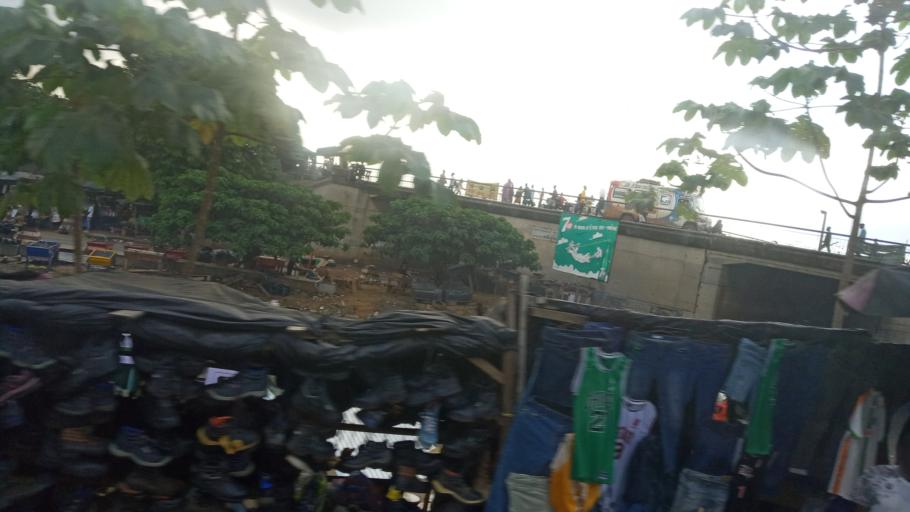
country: CI
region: Lagunes
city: Abidjan
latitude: 5.3597
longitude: -4.0286
